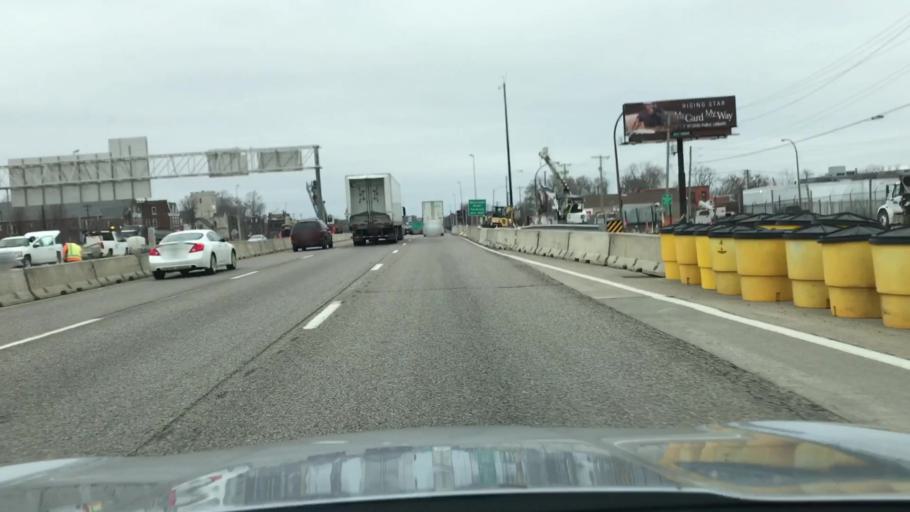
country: US
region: Missouri
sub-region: City of Saint Louis
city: St. Louis
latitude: 38.6486
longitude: -90.1916
